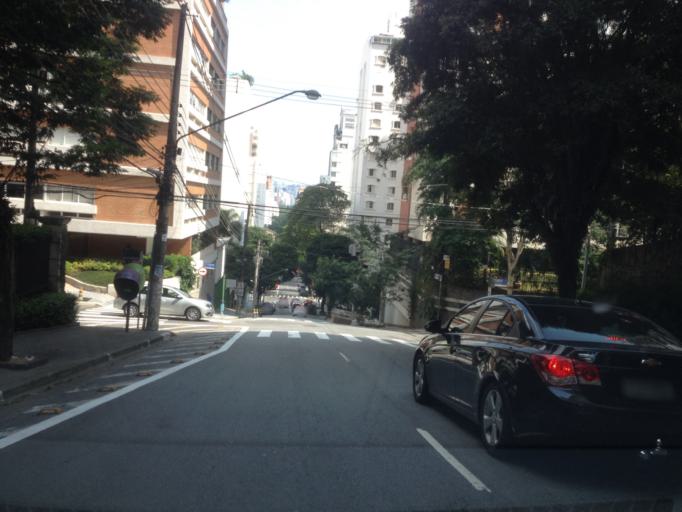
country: BR
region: Sao Paulo
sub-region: Sao Paulo
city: Sao Paulo
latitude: -23.5640
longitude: -46.6604
